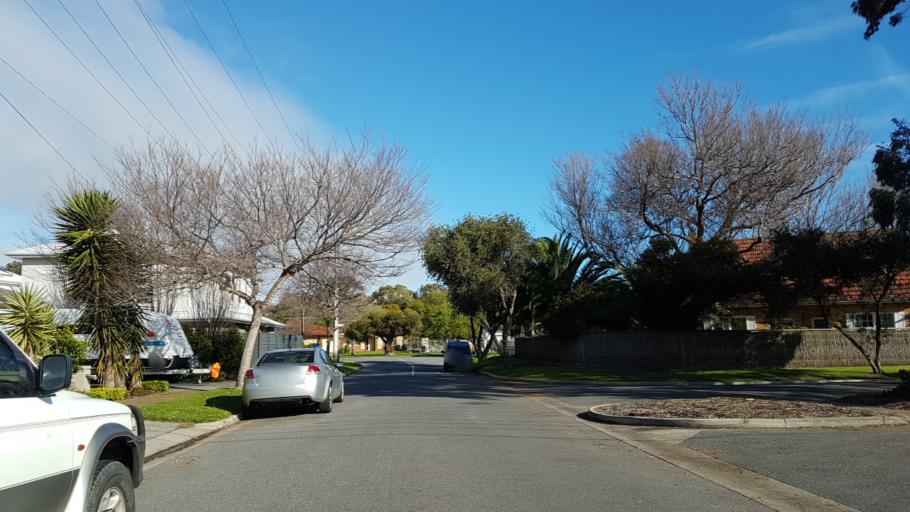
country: AU
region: South Australia
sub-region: Charles Sturt
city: Henley Beach
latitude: -34.9322
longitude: 138.5027
